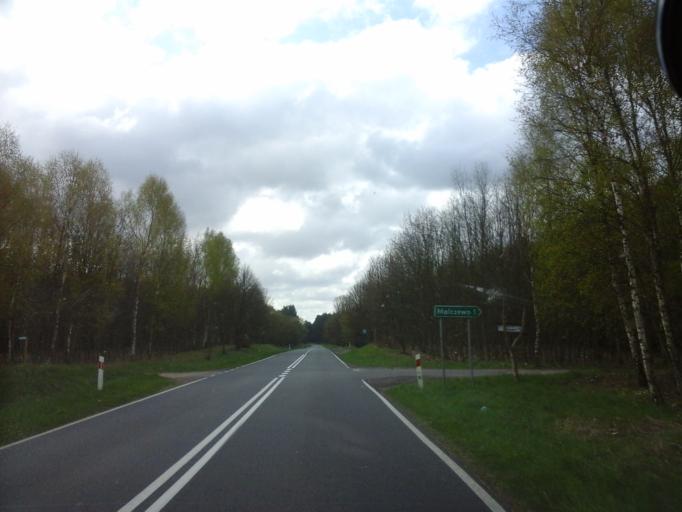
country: PL
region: West Pomeranian Voivodeship
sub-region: Powiat choszczenski
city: Bierzwnik
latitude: 53.0932
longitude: 15.6379
